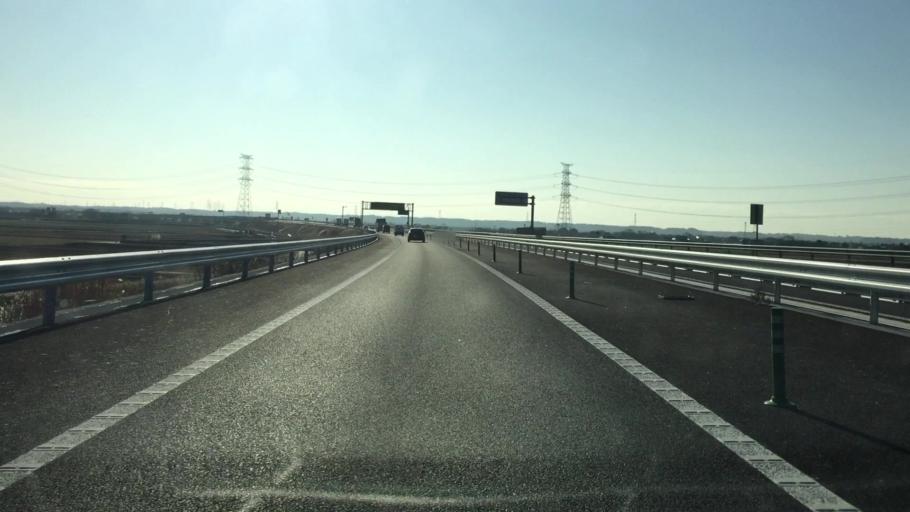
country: JP
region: Ibaraki
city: Inashiki
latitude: 35.9224
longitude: 140.3486
